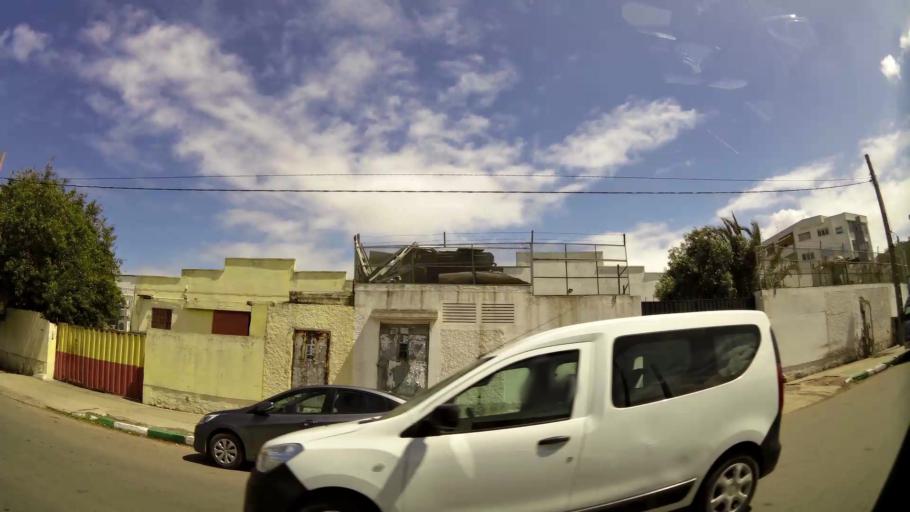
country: MA
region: Grand Casablanca
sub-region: Mediouna
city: Tit Mellil
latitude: 33.6004
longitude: -7.5204
